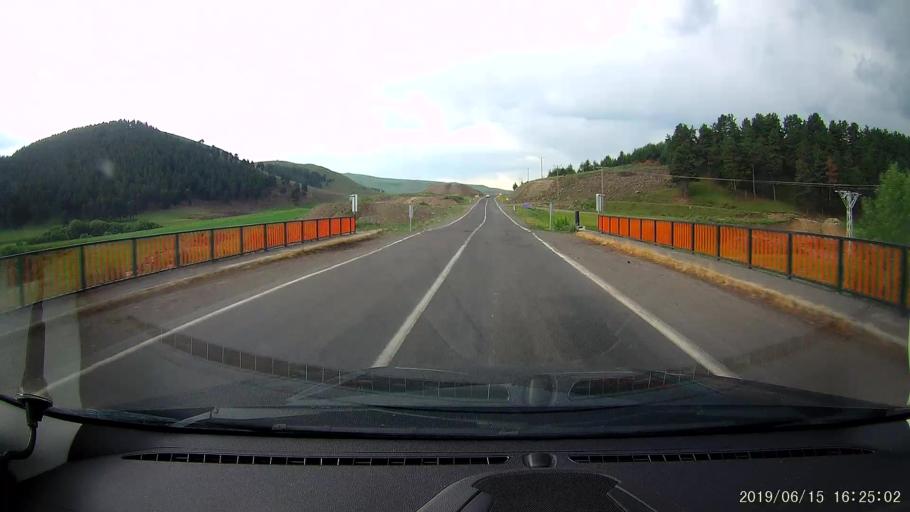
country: TR
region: Ardahan
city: Hanak
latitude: 41.1592
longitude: 42.8717
